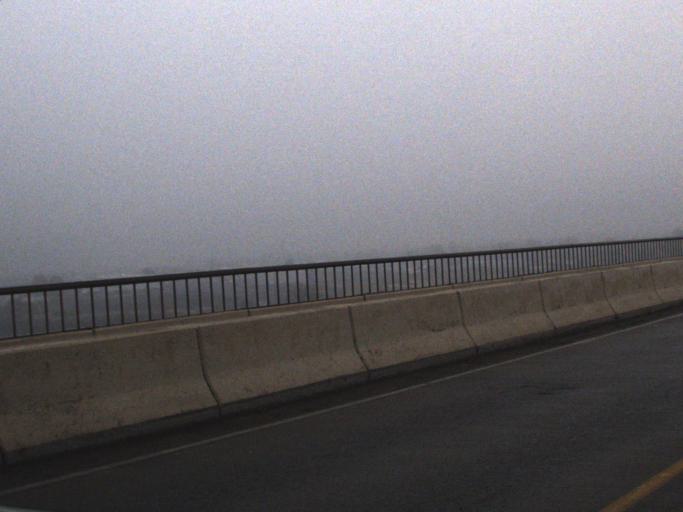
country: US
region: Washington
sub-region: Asotin County
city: West Clarkston-Highland
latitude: 46.4250
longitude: -117.0727
